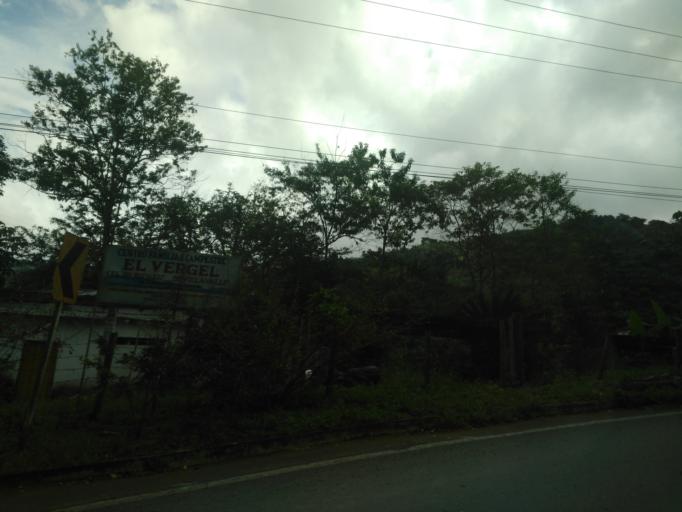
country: CO
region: Valle del Cauca
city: Sevilla
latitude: 4.2983
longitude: -75.8965
